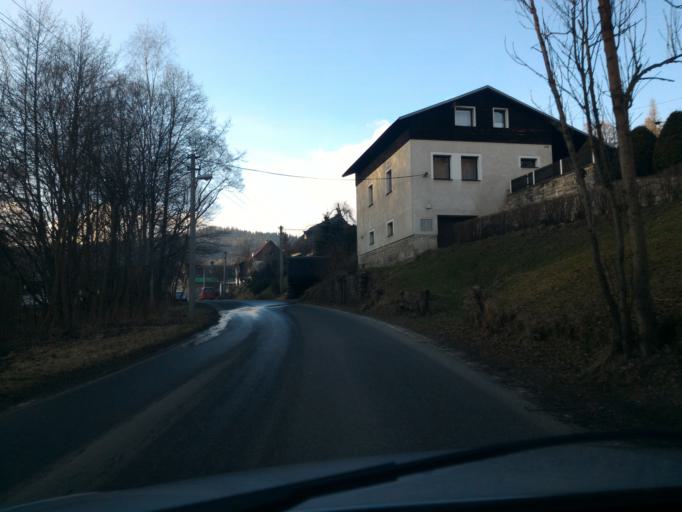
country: CZ
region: Liberecky
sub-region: Okres Jablonec nad Nisou
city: Smrzovka
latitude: 50.7388
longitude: 15.2742
